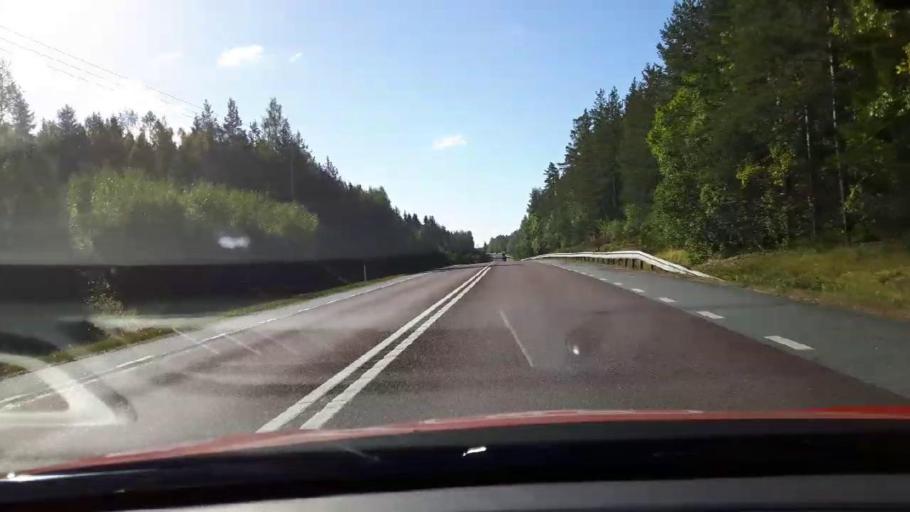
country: SE
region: Jaemtland
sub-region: Braecke Kommun
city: Braecke
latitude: 62.7993
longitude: 15.3717
